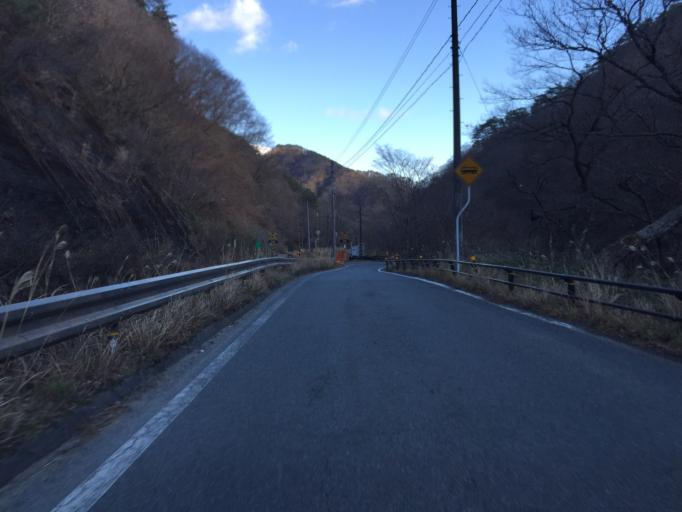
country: JP
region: Fukushima
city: Iwaki
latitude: 37.1995
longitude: 140.7765
